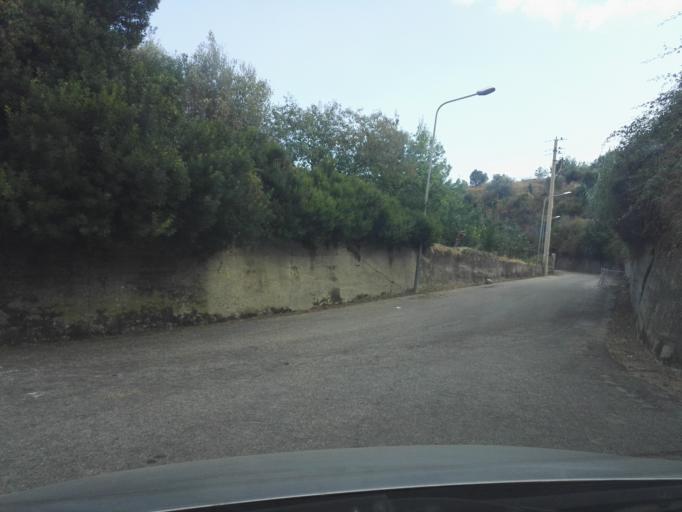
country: IT
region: Calabria
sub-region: Provincia di Reggio Calabria
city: Riace
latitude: 38.4164
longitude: 16.4816
